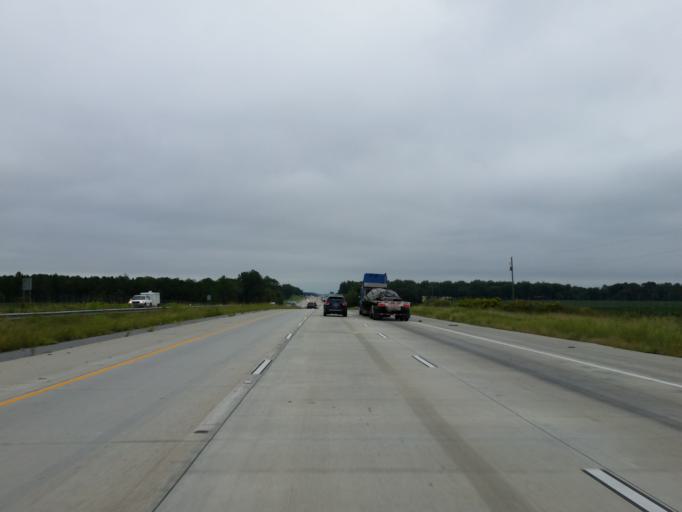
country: US
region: Georgia
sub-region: Dooly County
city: Vienna
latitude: 32.0355
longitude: -83.7636
